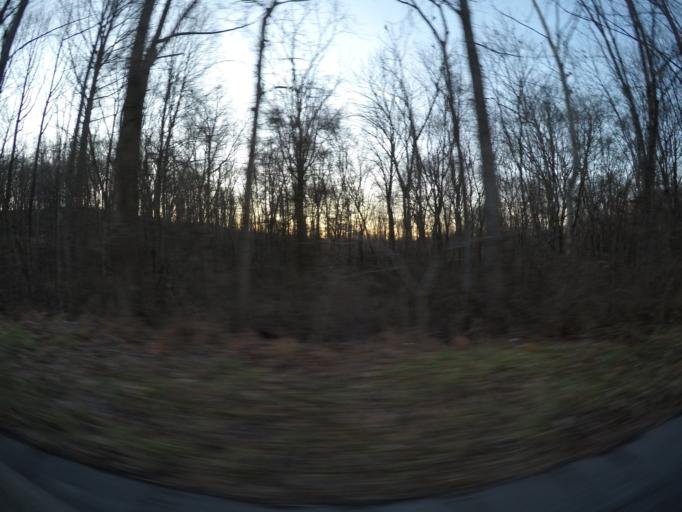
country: US
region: Maryland
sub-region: Cecil County
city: Rising Sun
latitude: 39.7068
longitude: -76.0650
